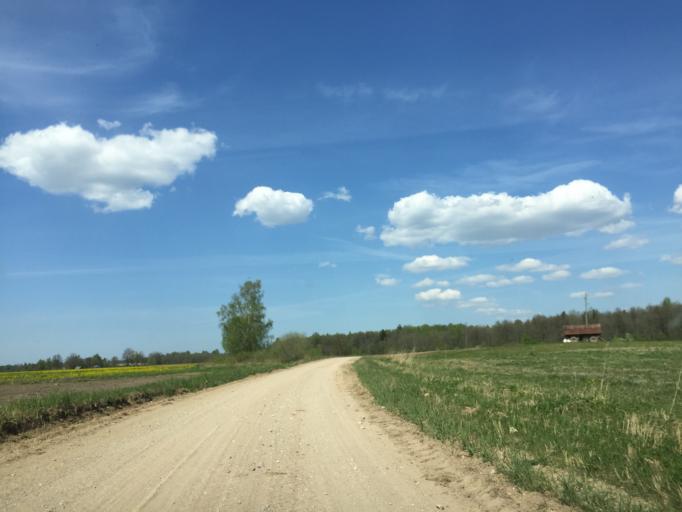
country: LV
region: Limbazu Rajons
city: Limbazi
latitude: 57.3763
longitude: 24.6281
